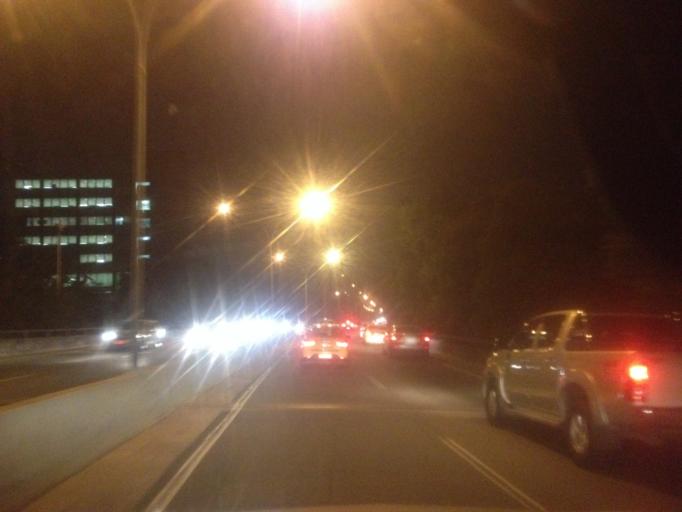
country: BR
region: Rio de Janeiro
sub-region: Rio De Janeiro
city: Rio de Janeiro
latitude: -22.9289
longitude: -43.2092
